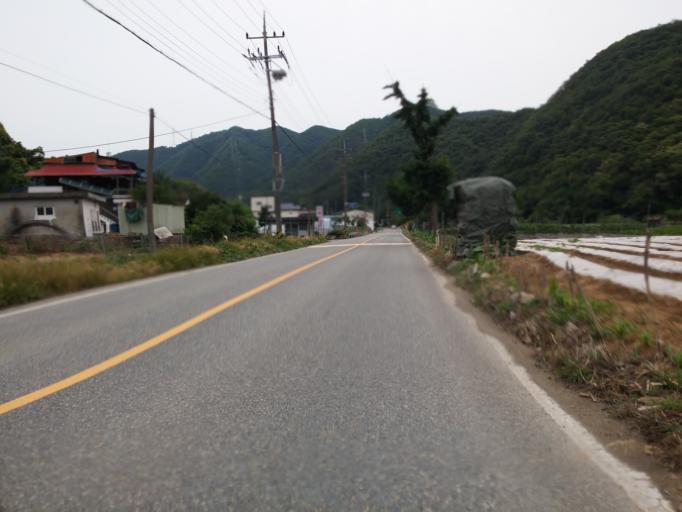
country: KR
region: Chungcheongbuk-do
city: Okcheon
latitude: 36.2564
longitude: 127.5146
